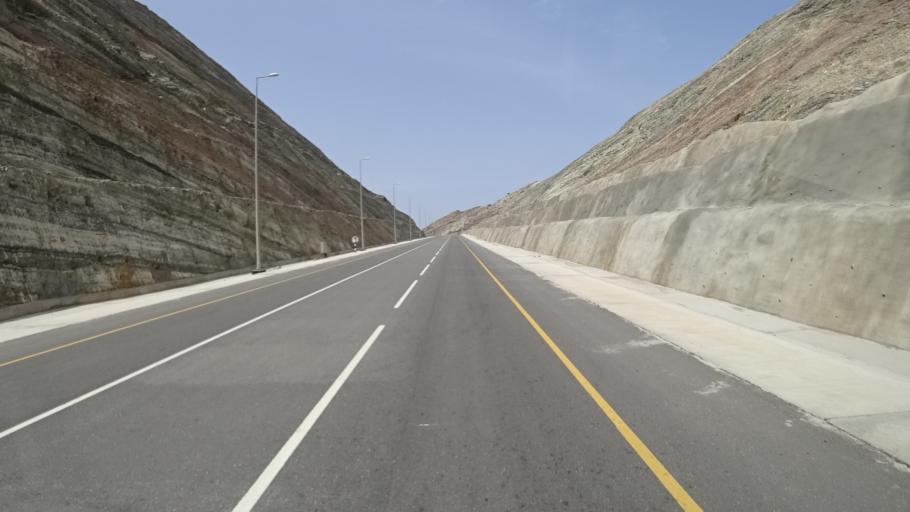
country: OM
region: Muhafazat Masqat
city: Muscat
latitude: 23.4407
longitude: 58.7583
